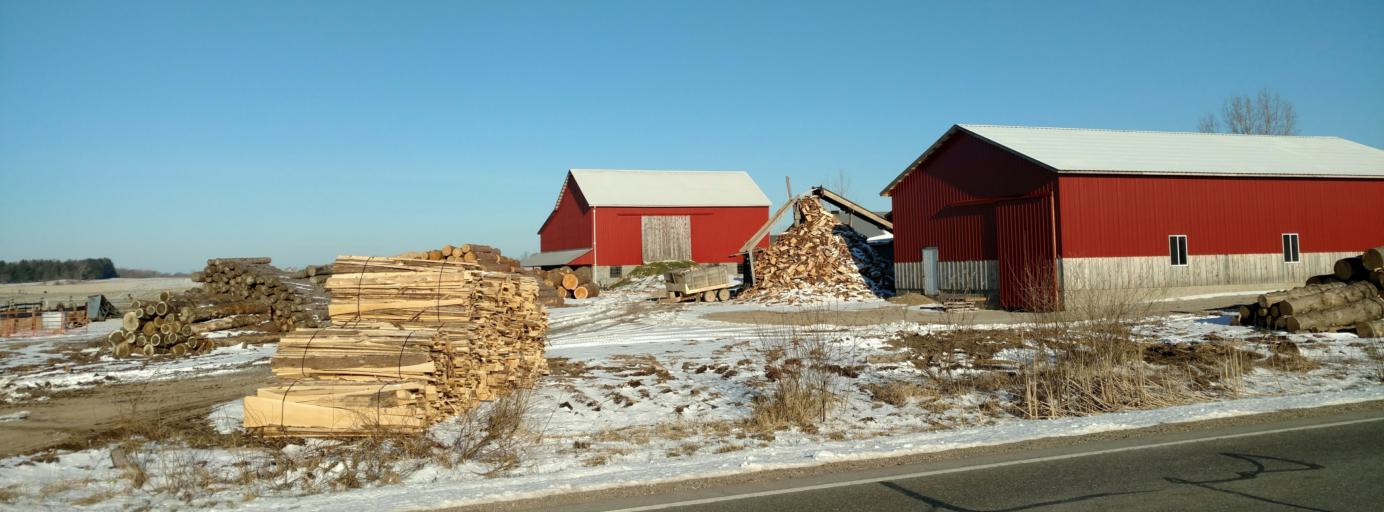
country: US
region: Michigan
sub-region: Gladwin County
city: Gladwin
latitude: 44.0425
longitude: -84.4866
